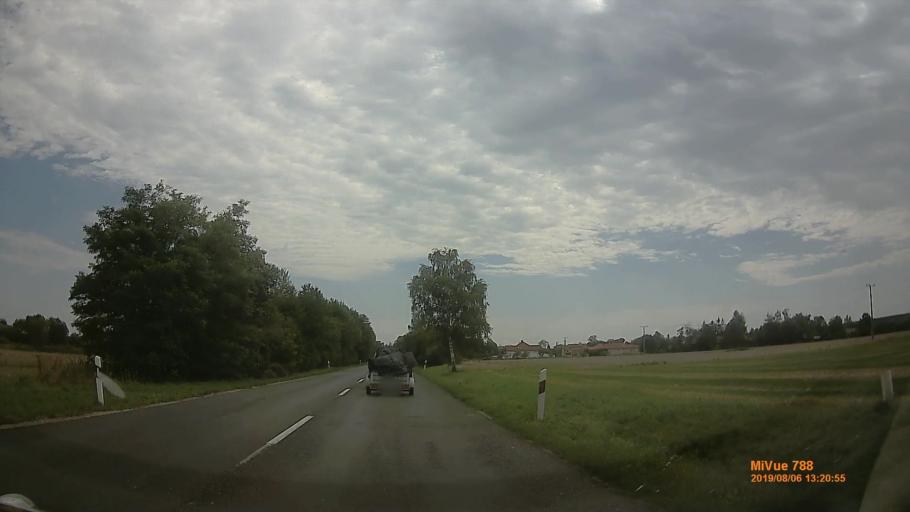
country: HU
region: Vas
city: Koszeg
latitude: 47.3479
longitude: 16.5732
